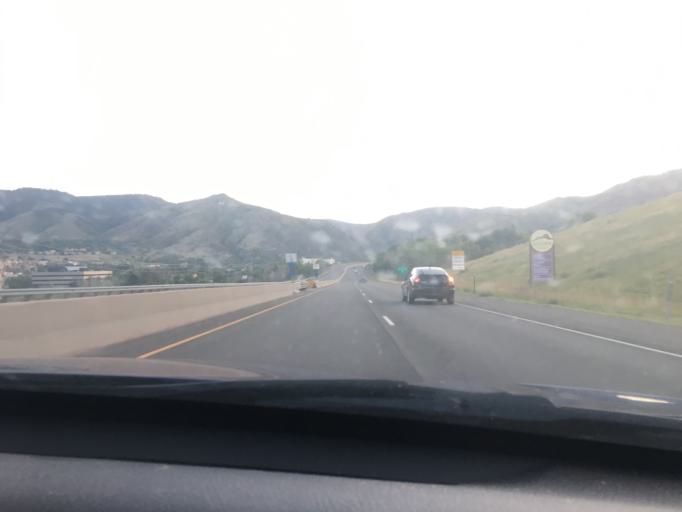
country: US
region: Colorado
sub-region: Jefferson County
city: Golden
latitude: 39.7643
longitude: -105.2143
